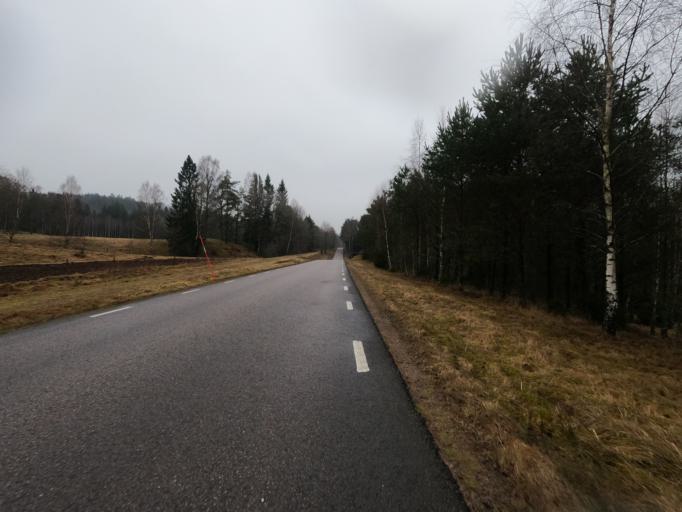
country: SE
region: Halland
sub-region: Hylte Kommun
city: Torup
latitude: 56.7759
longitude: 13.1786
